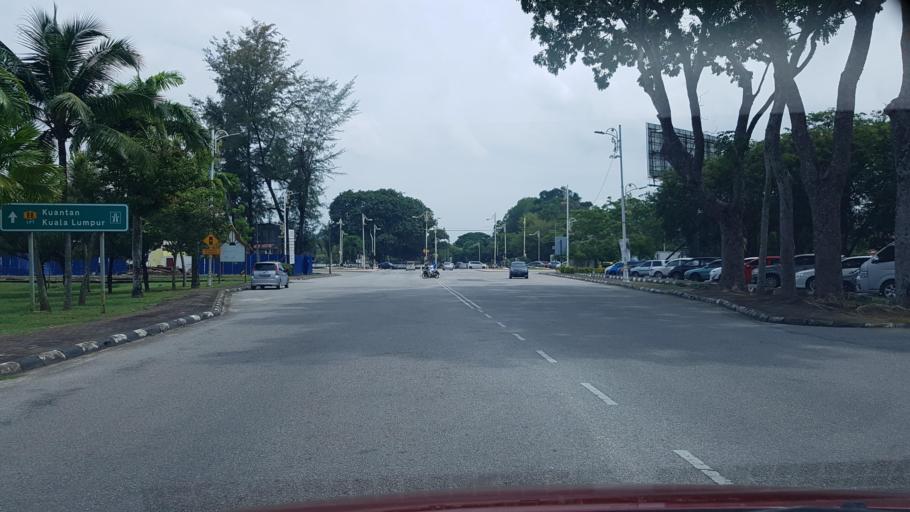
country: MY
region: Terengganu
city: Kuala Terengganu
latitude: 5.3196
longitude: 103.1546
